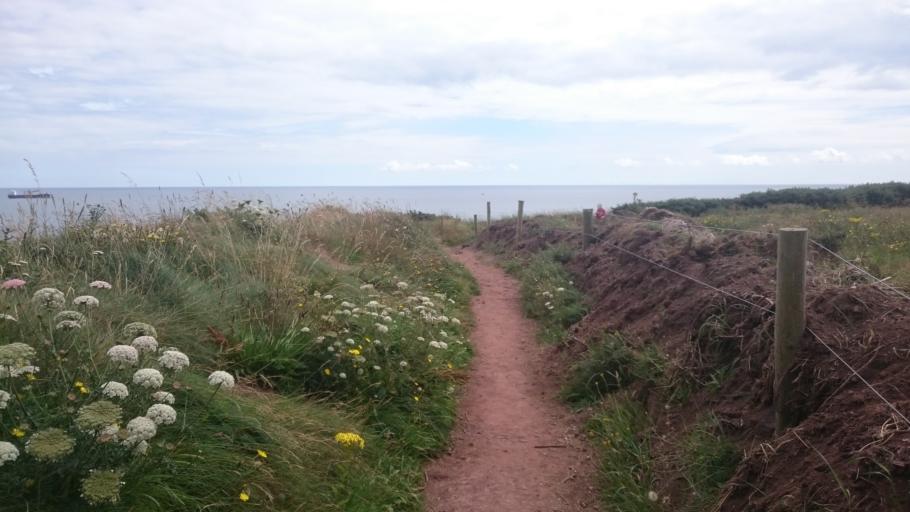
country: IE
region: Munster
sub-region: Waterford
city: Dunmore East
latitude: 52.1433
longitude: -6.9963
